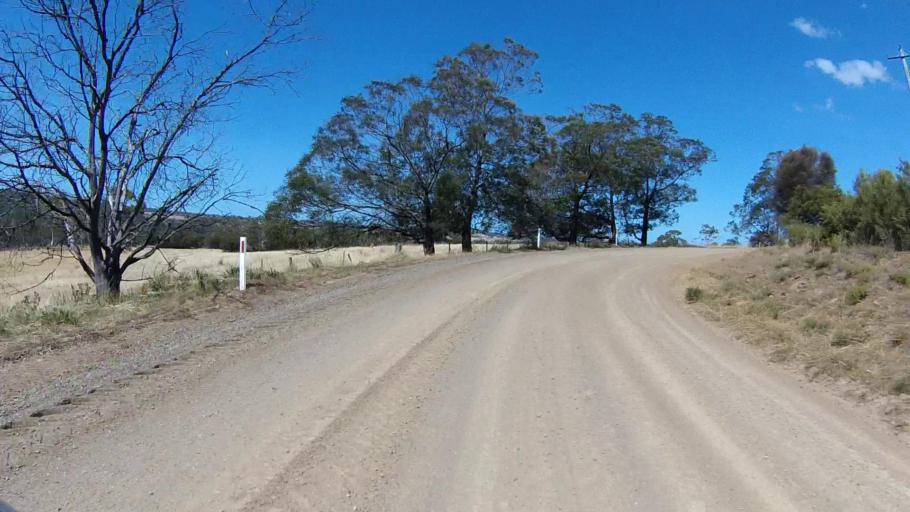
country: AU
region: Tasmania
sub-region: Break O'Day
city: St Helens
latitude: -41.9728
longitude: 148.0728
